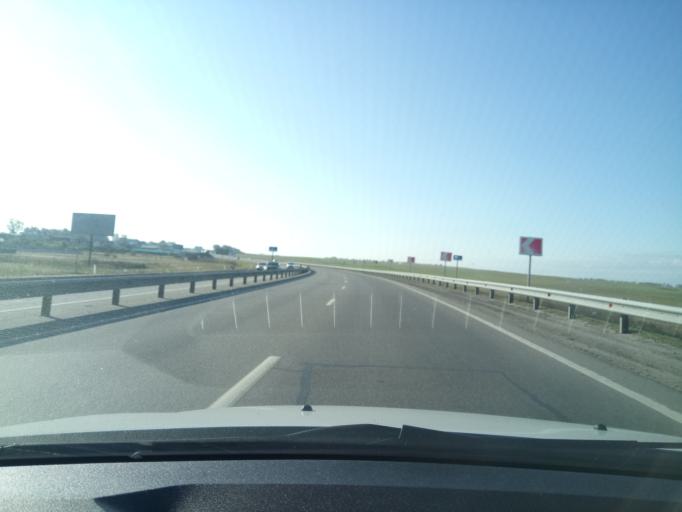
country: RU
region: Nizjnij Novgorod
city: Burevestnik
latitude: 56.1520
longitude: 43.9082
